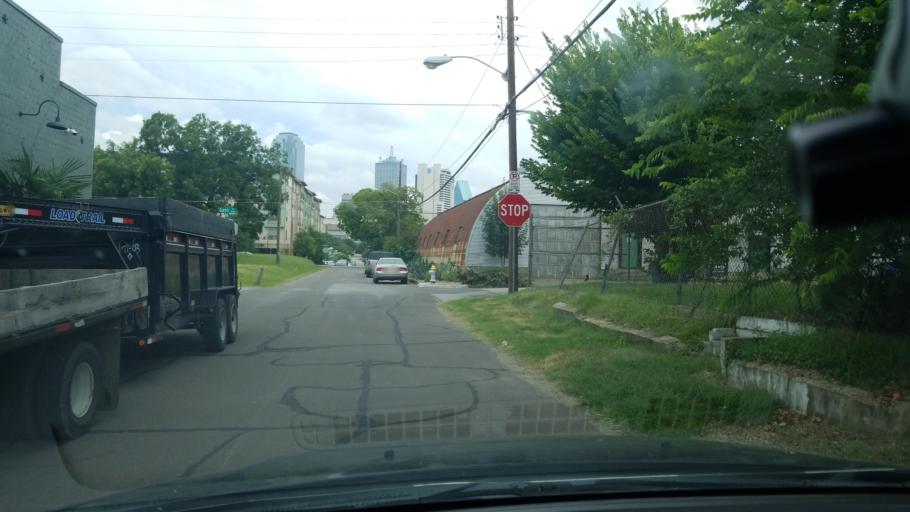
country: US
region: Texas
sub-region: Dallas County
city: Dallas
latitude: 32.7699
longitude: -96.7901
